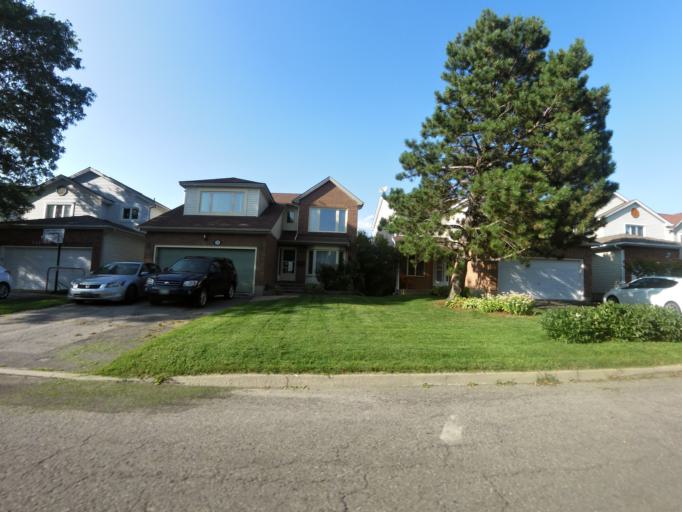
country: CA
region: Ontario
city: Clarence-Rockland
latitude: 45.4831
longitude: -75.4859
